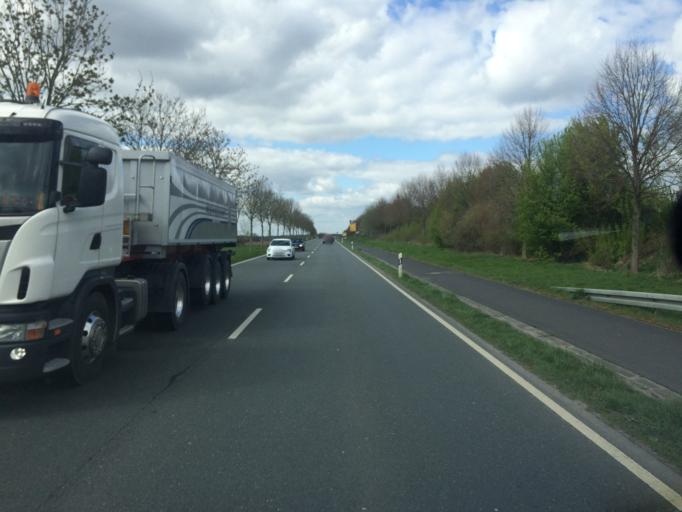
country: DE
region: North Rhine-Westphalia
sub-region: Regierungsbezirk Munster
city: Coesfeld
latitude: 51.9198
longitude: 7.1642
